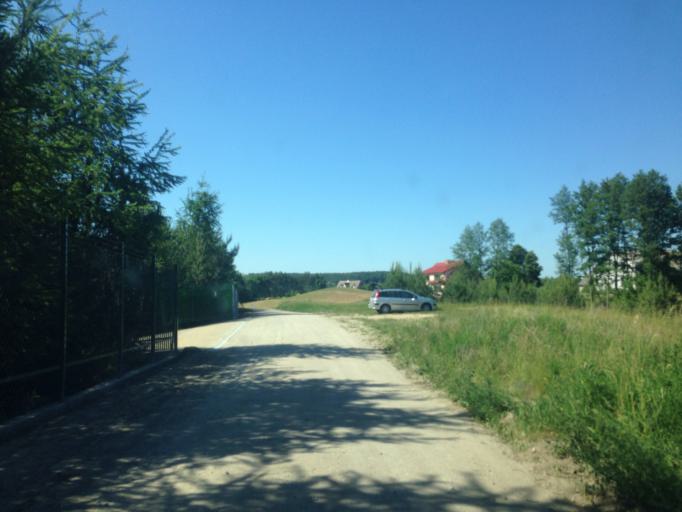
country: PL
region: Kujawsko-Pomorskie
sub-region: Powiat brodnicki
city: Gorzno
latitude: 53.2008
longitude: 19.6570
